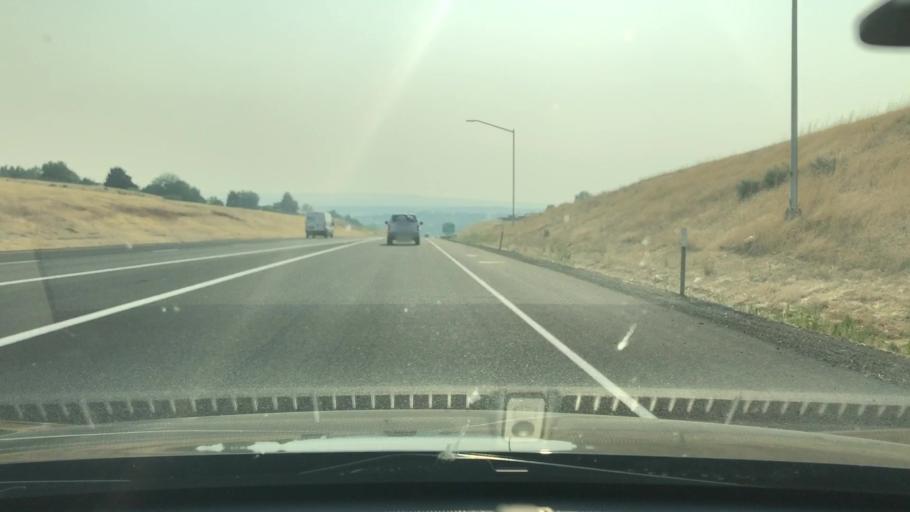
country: US
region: Oregon
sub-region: Umatilla County
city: Pendleton
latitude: 45.6630
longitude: -118.7824
